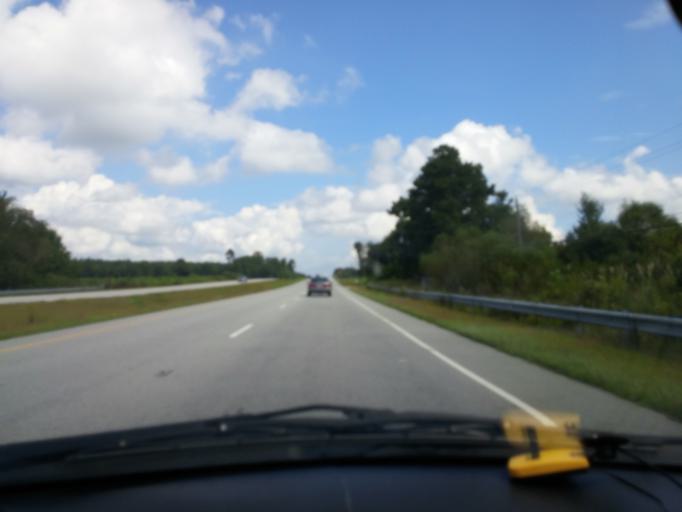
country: US
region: North Carolina
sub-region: Duplin County
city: Beulaville
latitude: 35.1065
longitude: -77.7206
